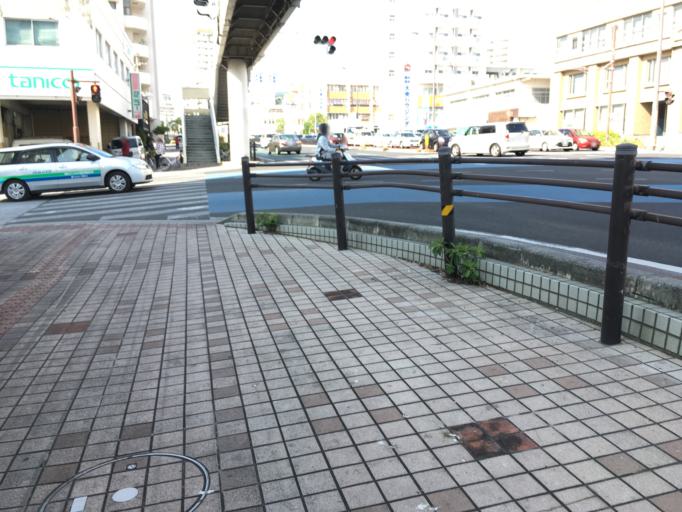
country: JP
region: Okinawa
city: Naha-shi
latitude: 26.2257
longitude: 127.6851
